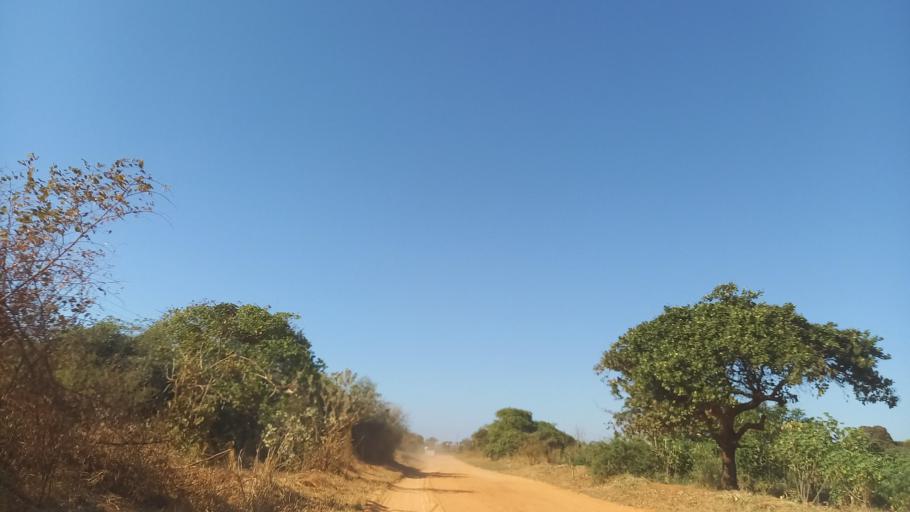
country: MZ
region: Cabo Delgado
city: Pemba
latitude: -13.1579
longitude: 40.5585
